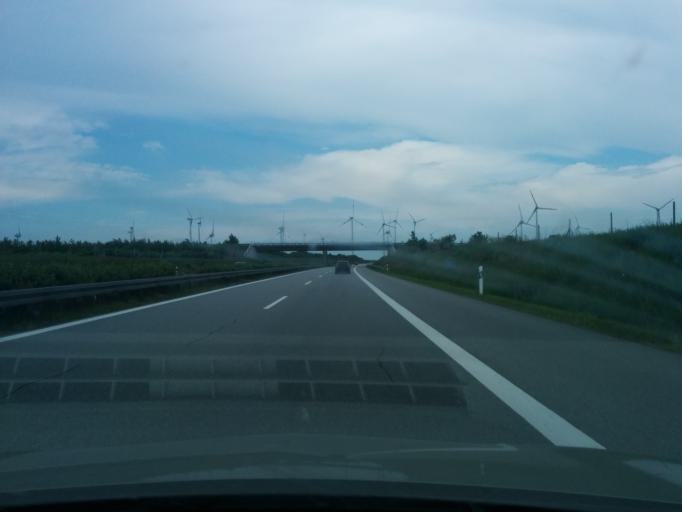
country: DE
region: Mecklenburg-Vorpommern
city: Kessin
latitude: 53.6945
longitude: 13.3256
